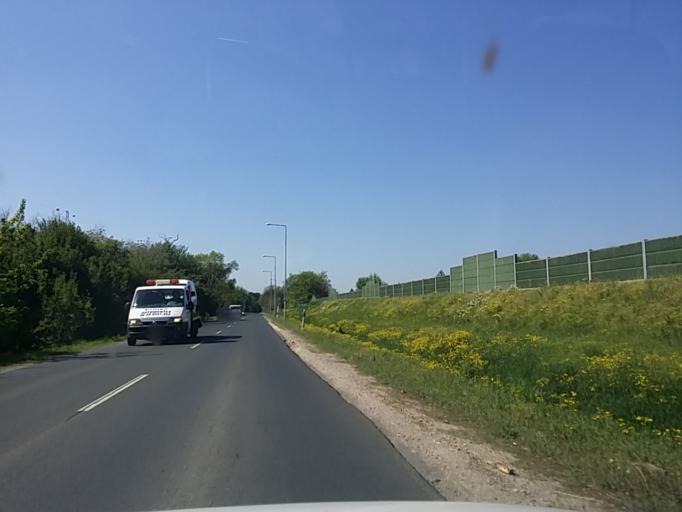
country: HU
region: Pest
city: Fot
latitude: 47.5954
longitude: 19.1761
